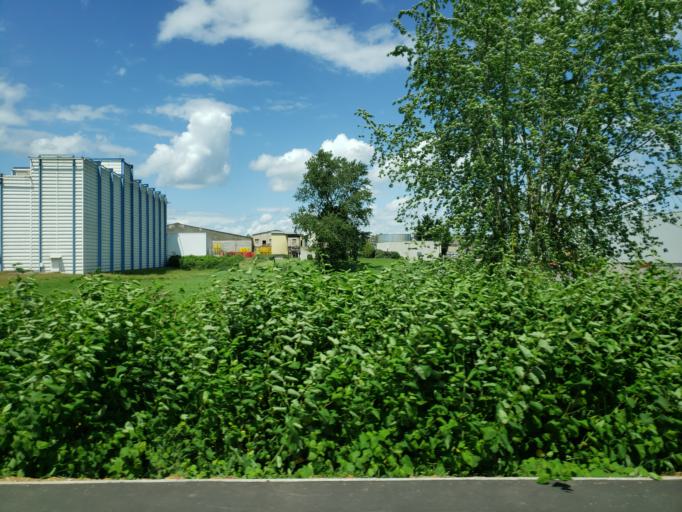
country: FR
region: Bourgogne
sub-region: Departement de l'Yonne
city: Migennes
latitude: 47.9568
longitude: 3.5064
